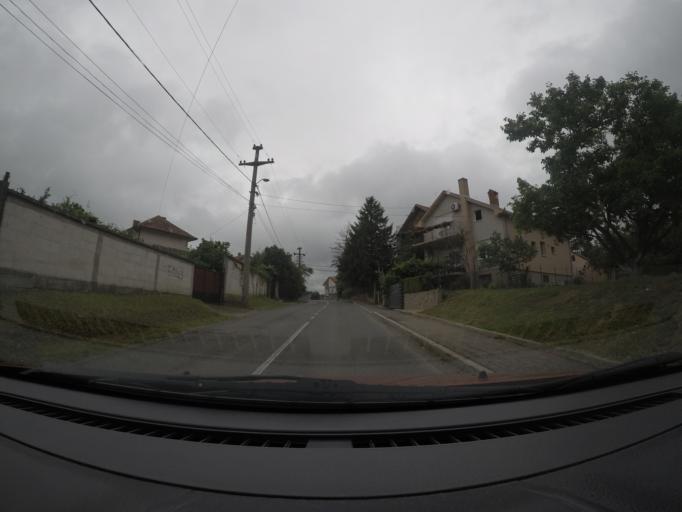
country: RS
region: Central Serbia
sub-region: Belgrade
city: Zvezdara
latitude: 44.6948
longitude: 20.5531
